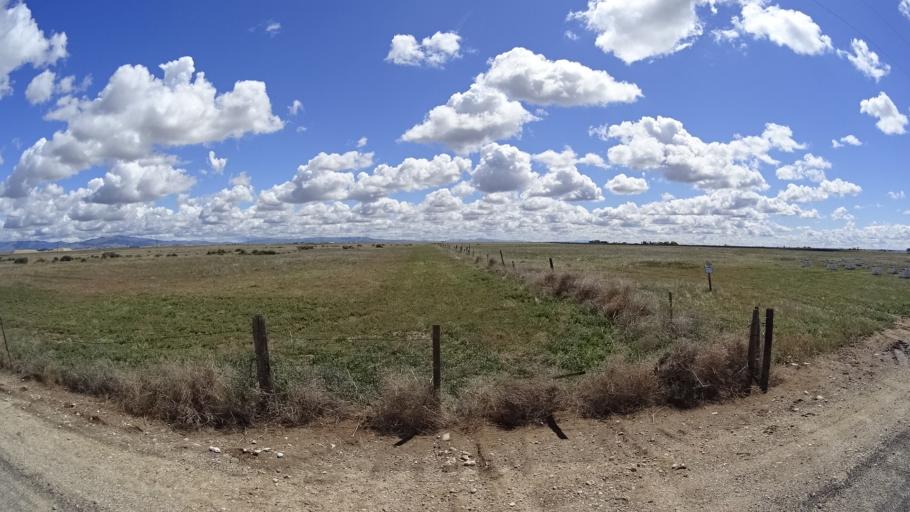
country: US
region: Idaho
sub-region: Ada County
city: Kuna
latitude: 43.4663
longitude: -116.2743
